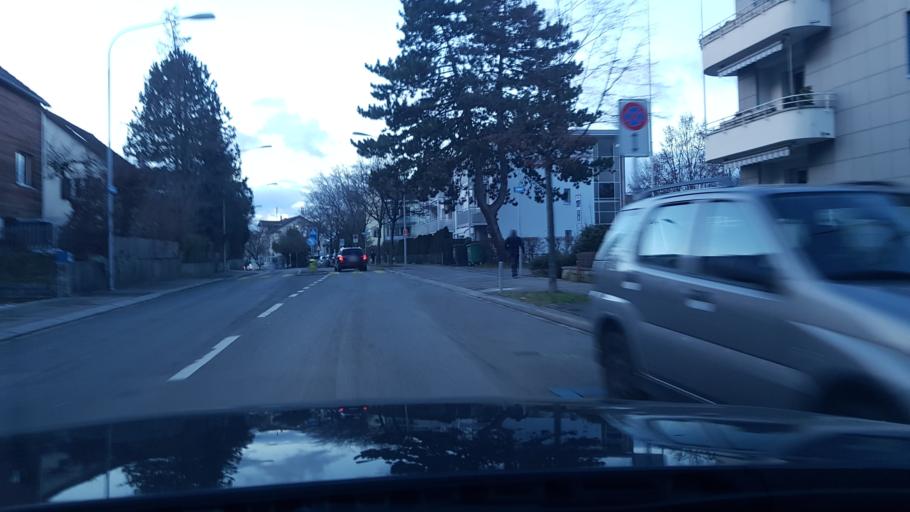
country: CH
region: Zurich
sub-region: Bezirk Zuerich
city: Zuerich (Kreis 9) / Albisrieden
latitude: 47.3712
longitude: 8.4887
